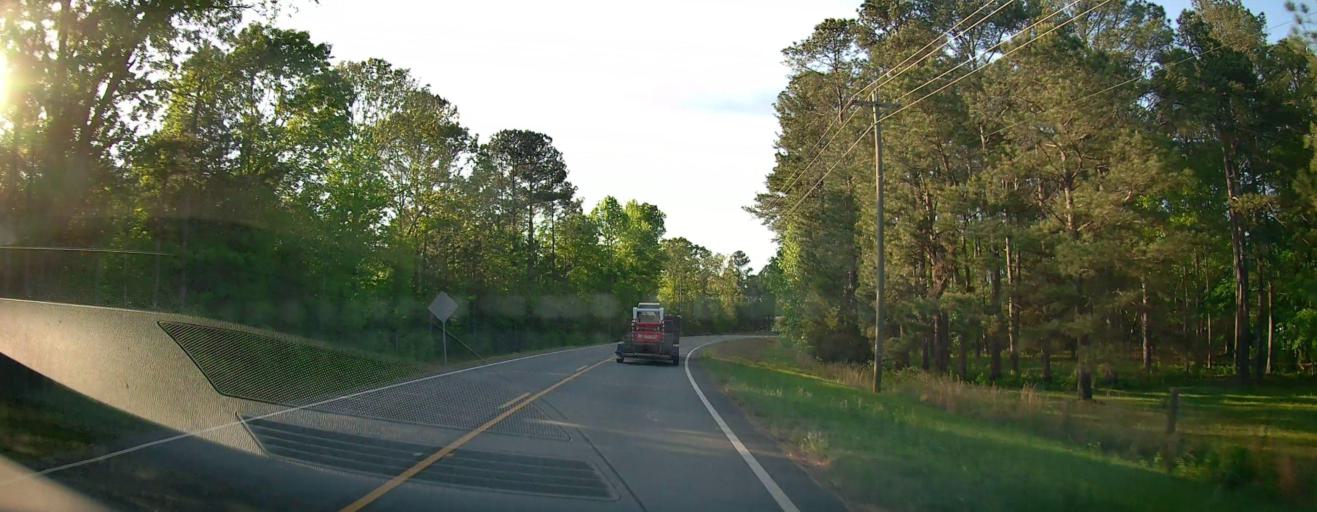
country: US
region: Georgia
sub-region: Putnam County
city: Eatonton
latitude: 33.3195
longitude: -83.4971
